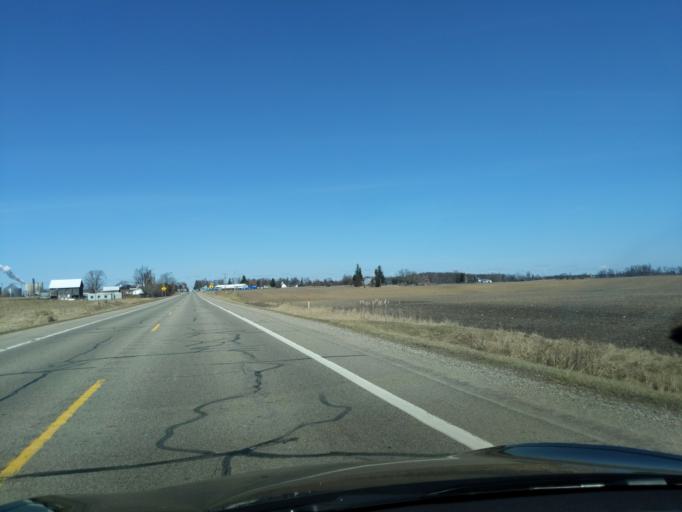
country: US
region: Michigan
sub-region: Ionia County
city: Lake Odessa
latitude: 42.7505
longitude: -85.0745
